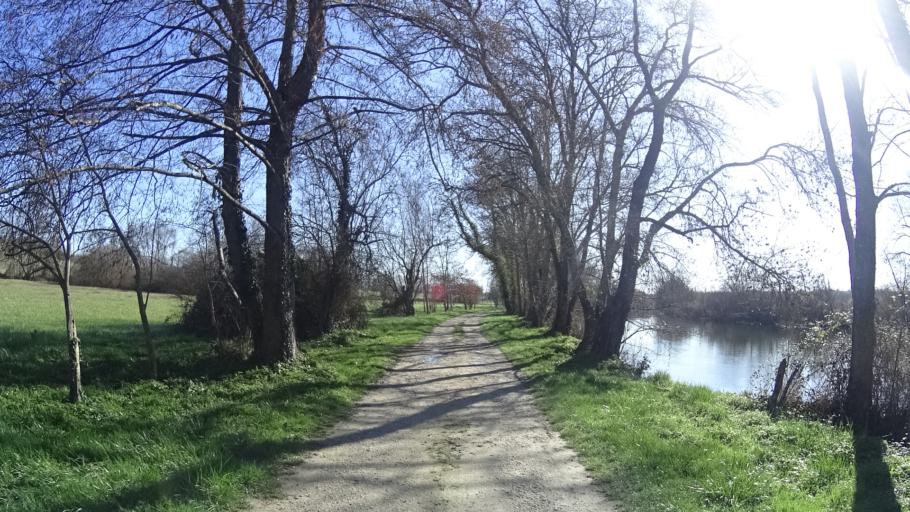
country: FR
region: Aquitaine
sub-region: Departement de la Dordogne
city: Saint-Aulaye
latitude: 45.2197
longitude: 0.1079
